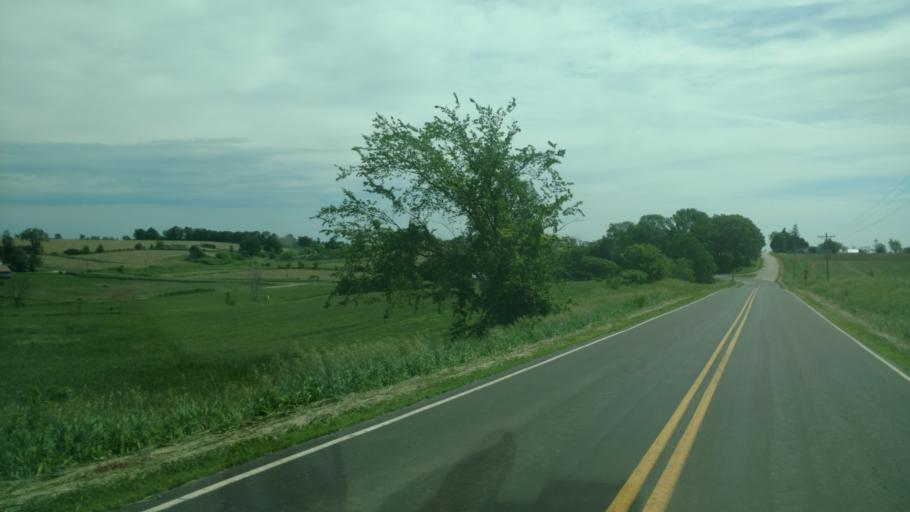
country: US
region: Wisconsin
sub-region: Vernon County
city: Hillsboro
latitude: 43.7115
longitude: -90.4514
